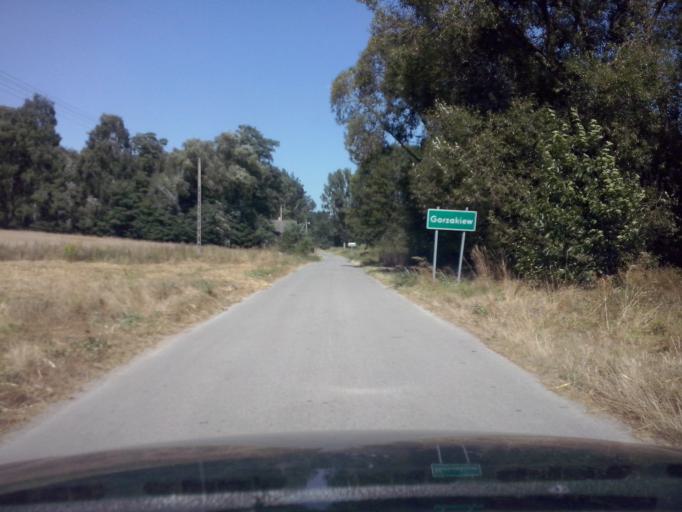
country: PL
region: Swietokrzyskie
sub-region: Powiat buski
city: Gnojno
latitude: 50.6135
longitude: 20.8890
